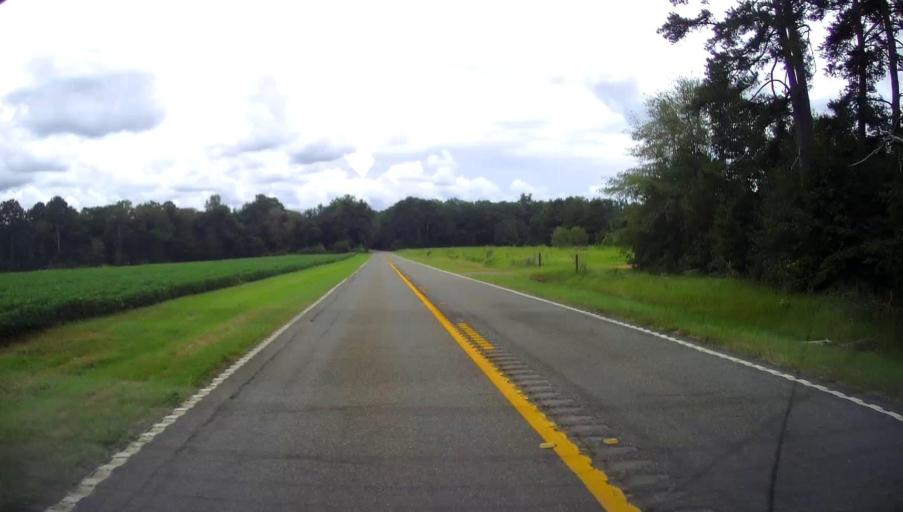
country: US
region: Georgia
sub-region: Dooly County
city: Unadilla
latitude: 32.2872
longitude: -83.8266
